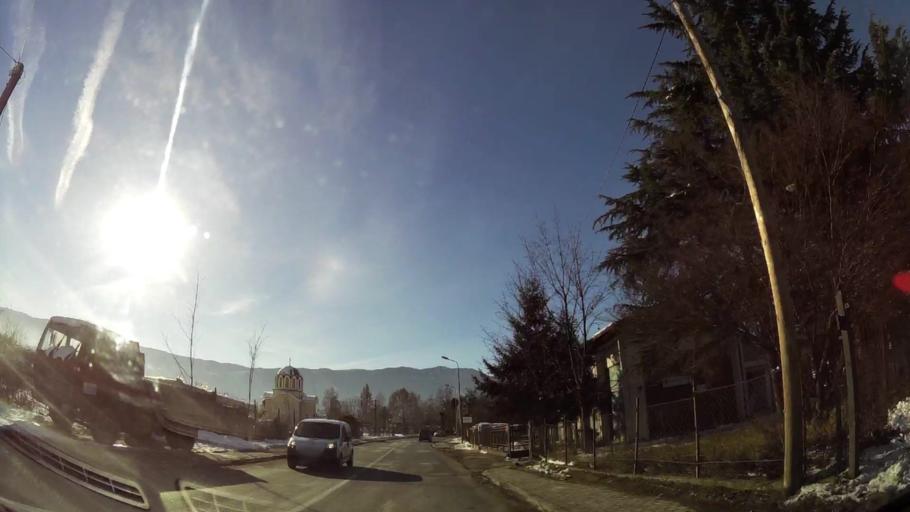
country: MK
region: Saraj
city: Saraj
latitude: 42.0052
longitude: 21.3326
